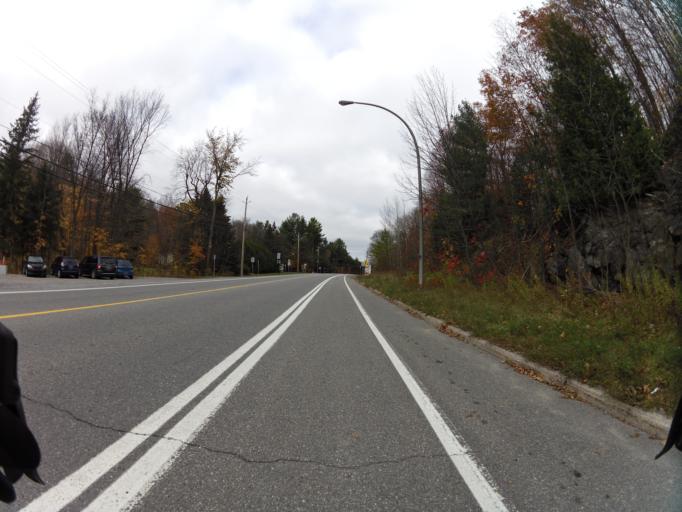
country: CA
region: Quebec
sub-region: Outaouais
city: Gatineau
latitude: 45.5174
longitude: -75.8087
